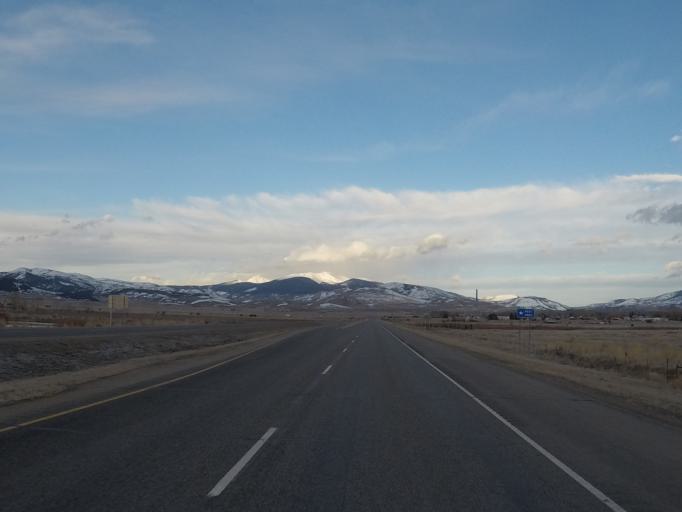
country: US
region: Montana
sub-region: Deer Lodge County
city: Warm Springs
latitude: 46.0956
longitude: -112.8061
